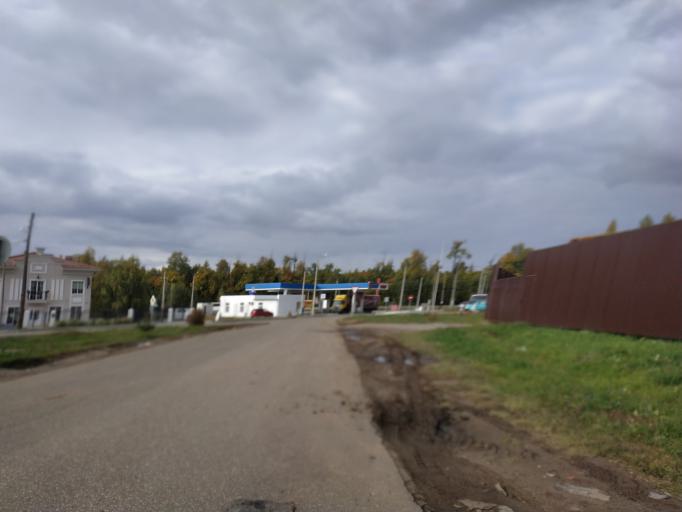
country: RU
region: Chuvashia
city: Ishley
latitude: 56.1323
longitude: 47.0867
